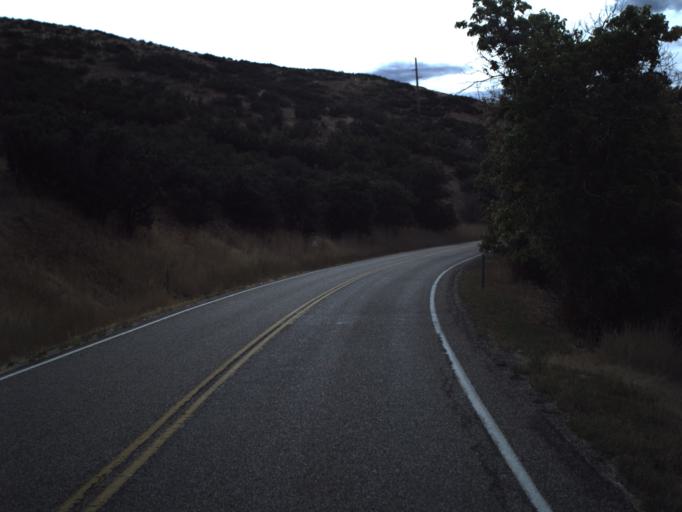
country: US
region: Utah
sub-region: Morgan County
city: Morgan
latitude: 40.9442
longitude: -111.6484
